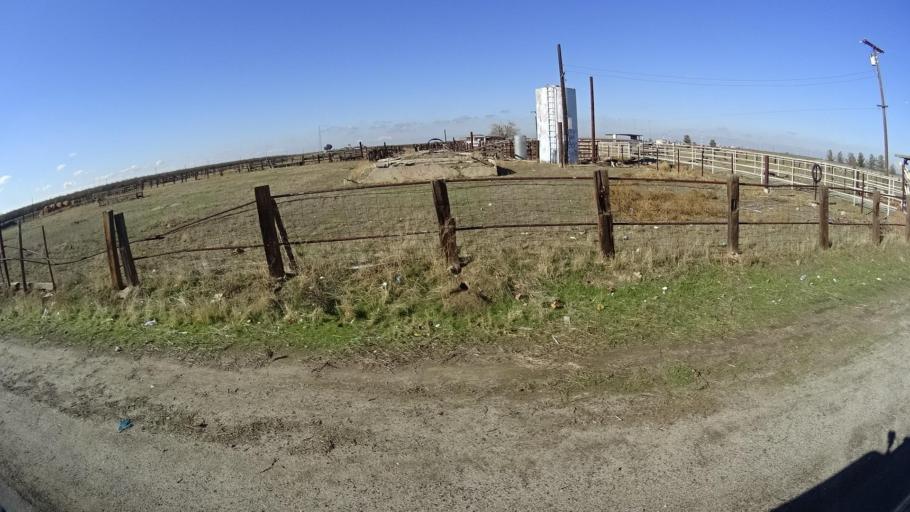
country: US
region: California
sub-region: Kern County
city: Delano
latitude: 35.7422
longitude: -119.2584
